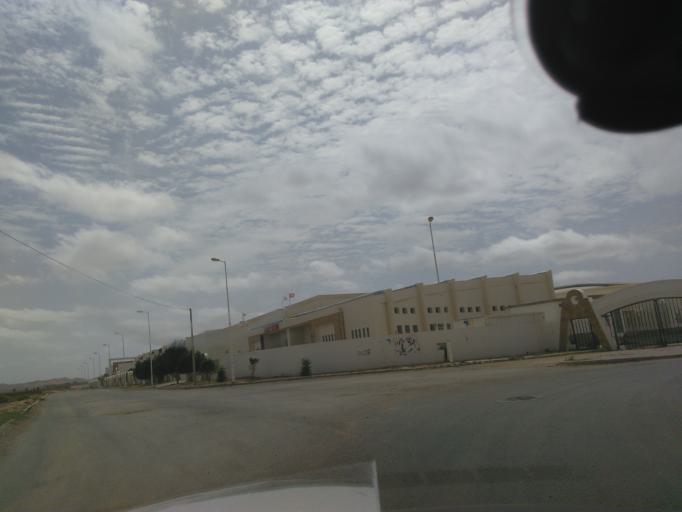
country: TN
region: Tataouine
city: Tataouine
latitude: 32.9505
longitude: 10.4724
